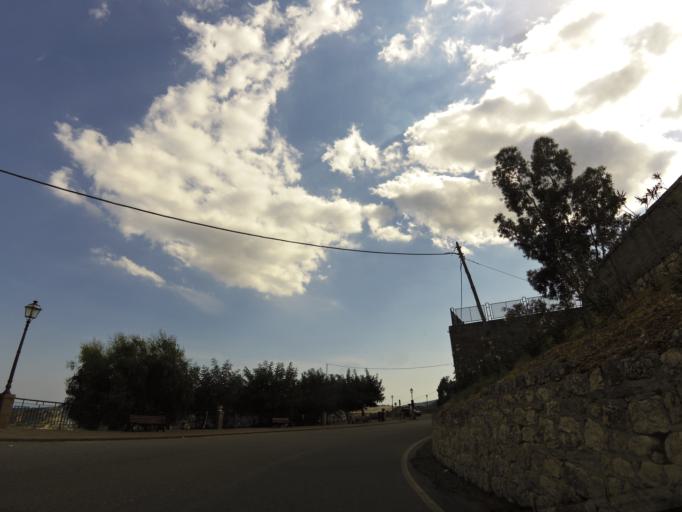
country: IT
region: Calabria
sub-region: Provincia di Reggio Calabria
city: Stilo
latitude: 38.4767
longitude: 16.4709
